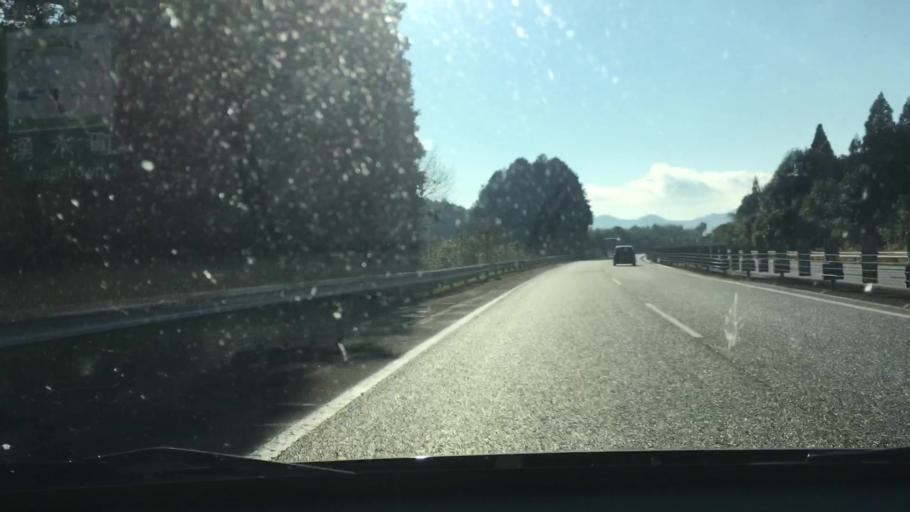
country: JP
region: Kagoshima
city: Okuchi-shinohara
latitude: 32.0184
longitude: 130.7708
